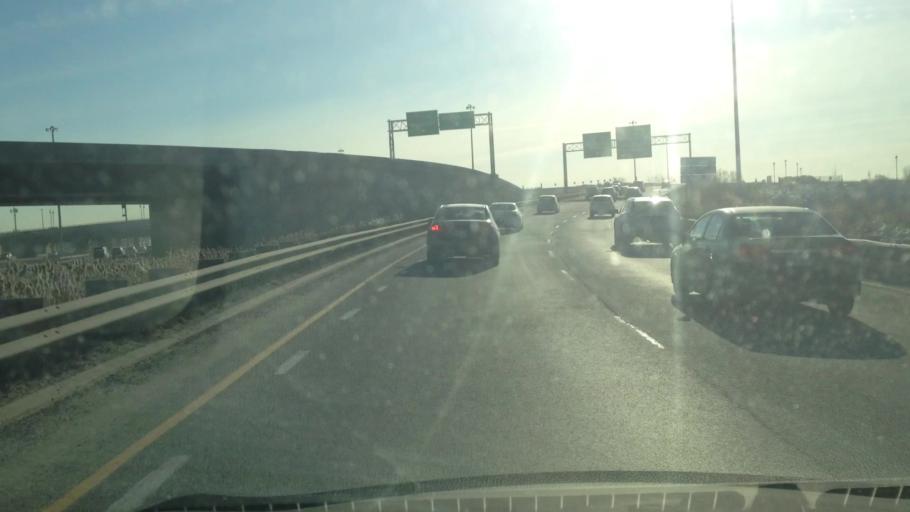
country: CA
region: Quebec
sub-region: Laurentides
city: Boisbriand
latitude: 45.6296
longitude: -73.8445
